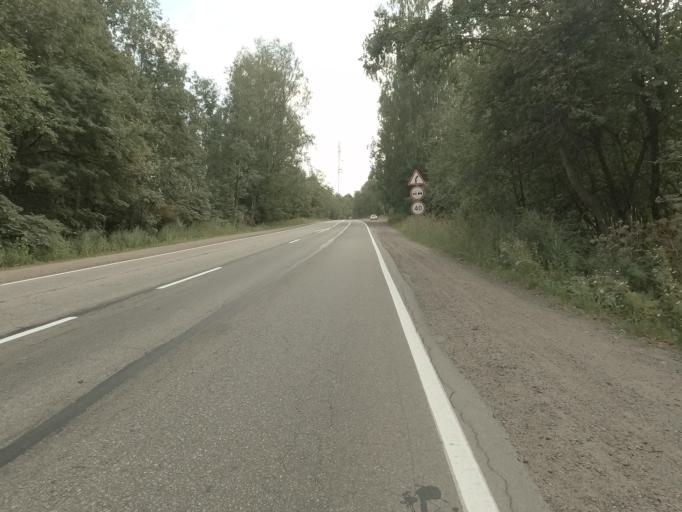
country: RU
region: Leningrad
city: Kamennogorsk
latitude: 60.8621
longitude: 28.9706
